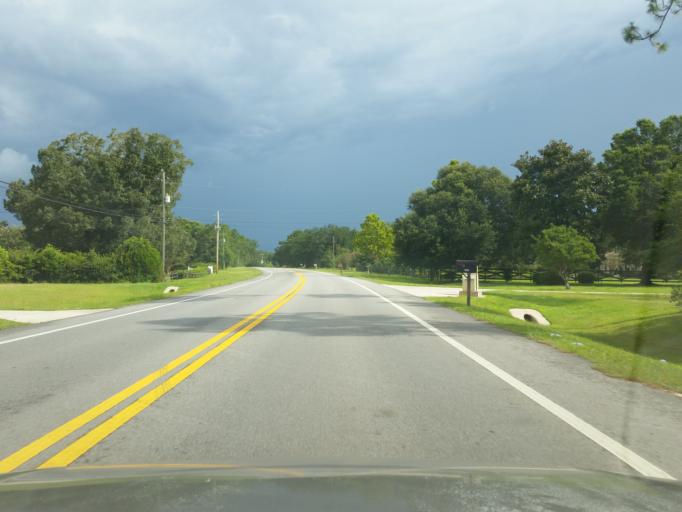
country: US
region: Florida
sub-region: Escambia County
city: Gonzalez
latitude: 30.5379
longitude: -87.3260
